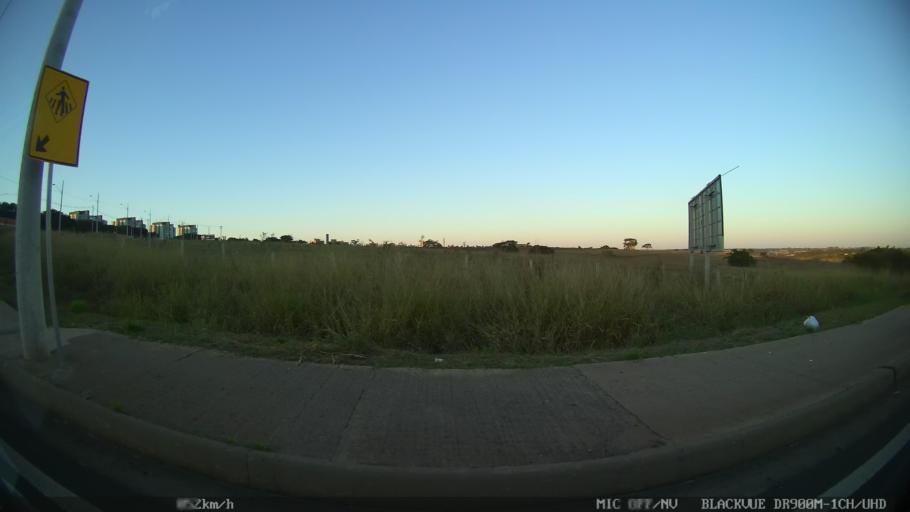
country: BR
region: Sao Paulo
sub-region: Sao Jose Do Rio Preto
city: Sao Jose do Rio Preto
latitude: -20.8568
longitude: -49.4042
